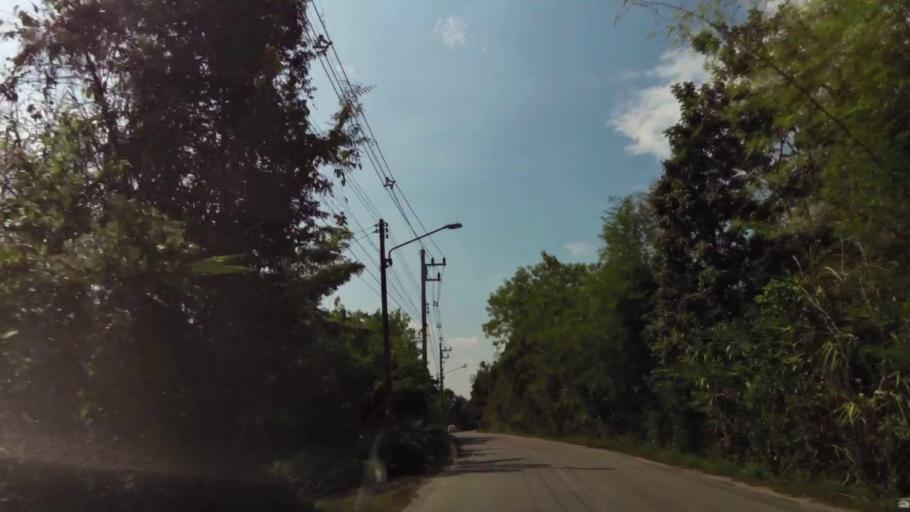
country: TH
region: Chiang Rai
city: Chiang Rai
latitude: 19.8871
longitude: 99.8117
